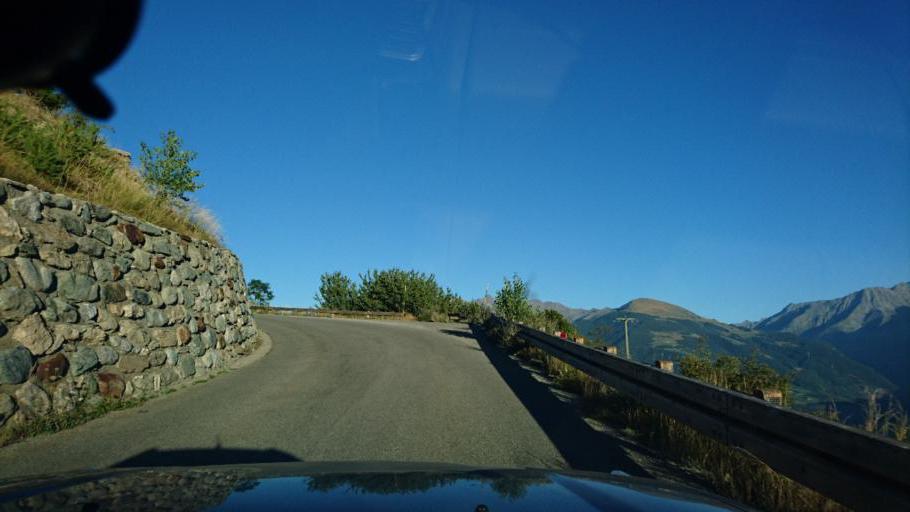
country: IT
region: Aosta Valley
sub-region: Valle d'Aosta
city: Saint-Nicolas
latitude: 45.7279
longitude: 7.1861
